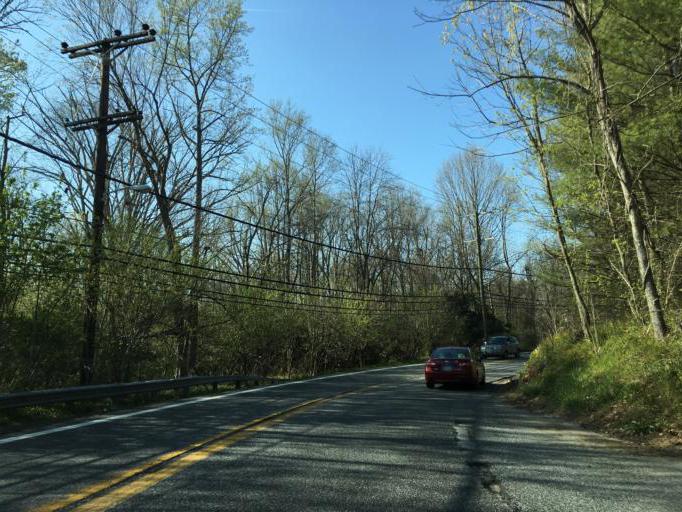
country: US
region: Maryland
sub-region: Baltimore County
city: Hunt Valley
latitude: 39.4958
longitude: -76.6425
